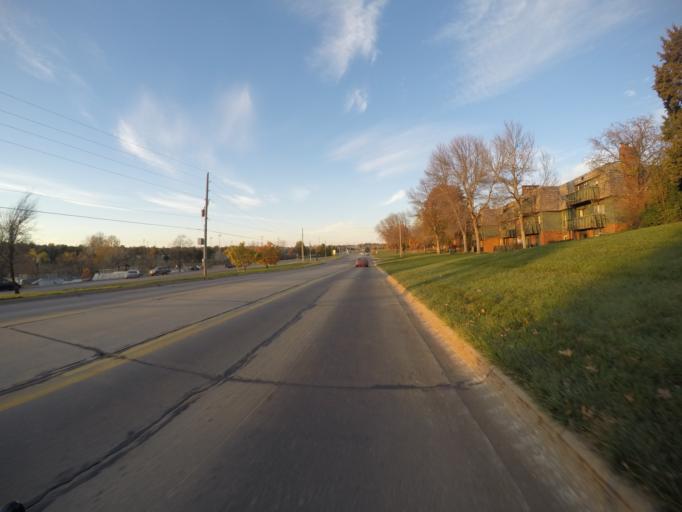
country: US
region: Kansas
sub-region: Riley County
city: Manhattan
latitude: 39.1999
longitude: -96.6168
